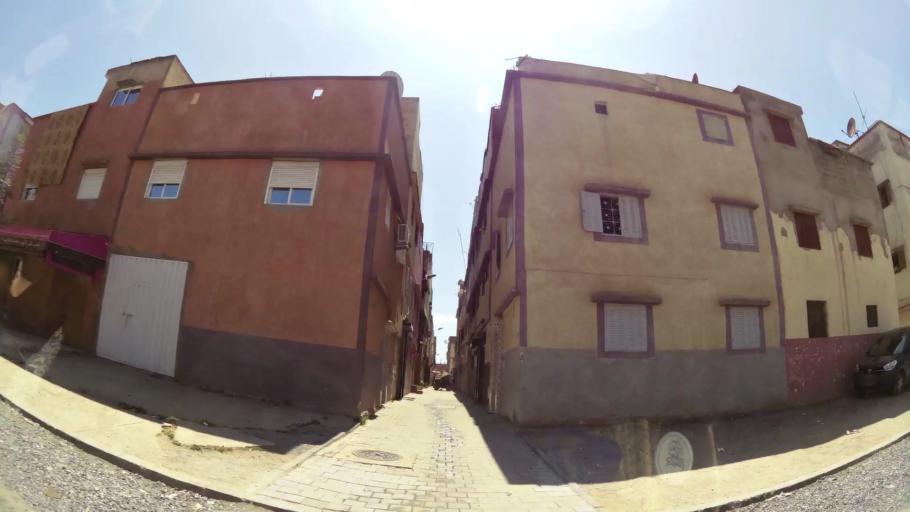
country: MA
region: Gharb-Chrarda-Beni Hssen
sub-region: Kenitra Province
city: Kenitra
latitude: 34.2532
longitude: -6.5428
